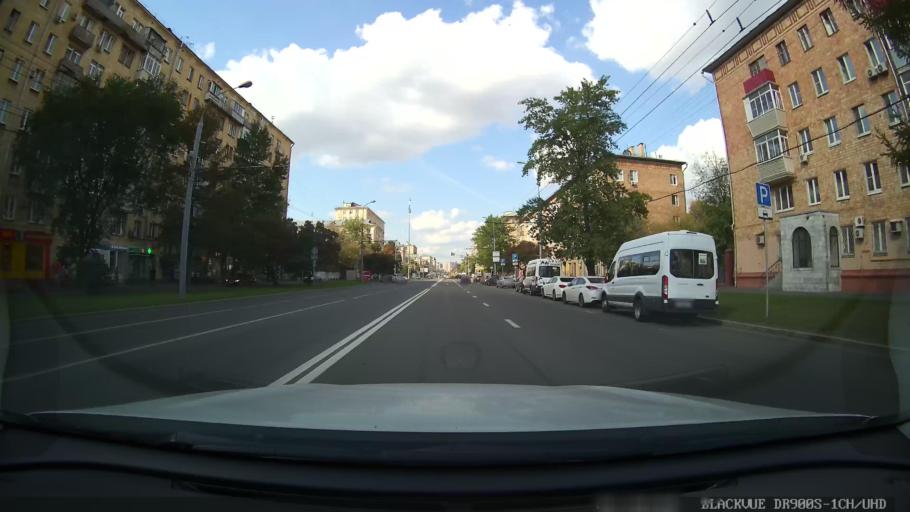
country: RU
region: Moscow
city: Sokol
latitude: 55.7756
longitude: 37.5189
